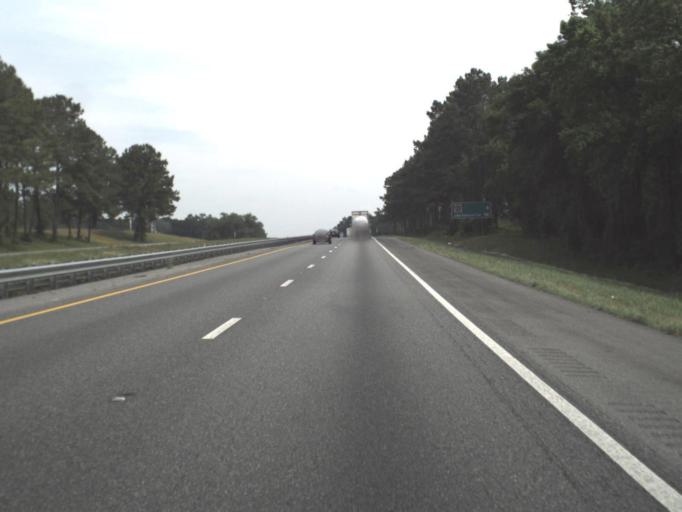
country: US
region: Florida
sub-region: Suwannee County
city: Live Oak
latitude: 30.3214
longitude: -82.9501
